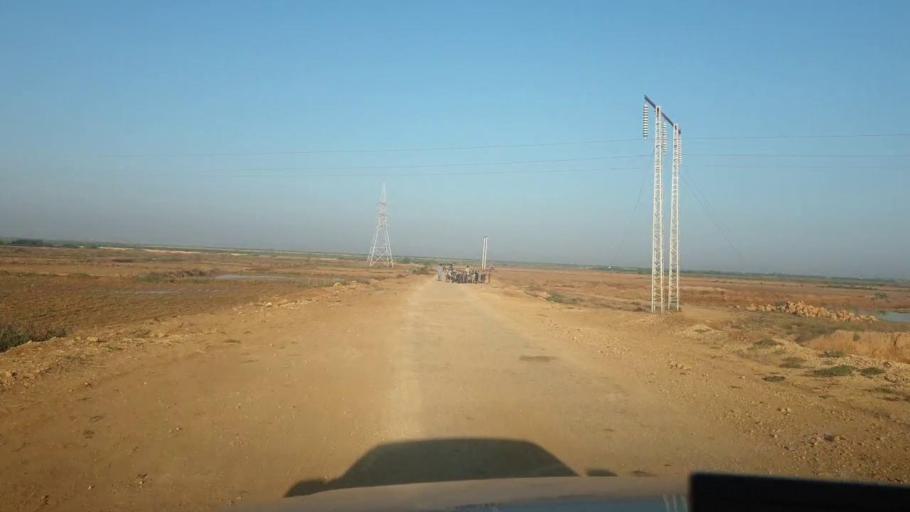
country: PK
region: Sindh
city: Thatta
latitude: 24.6997
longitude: 67.8555
